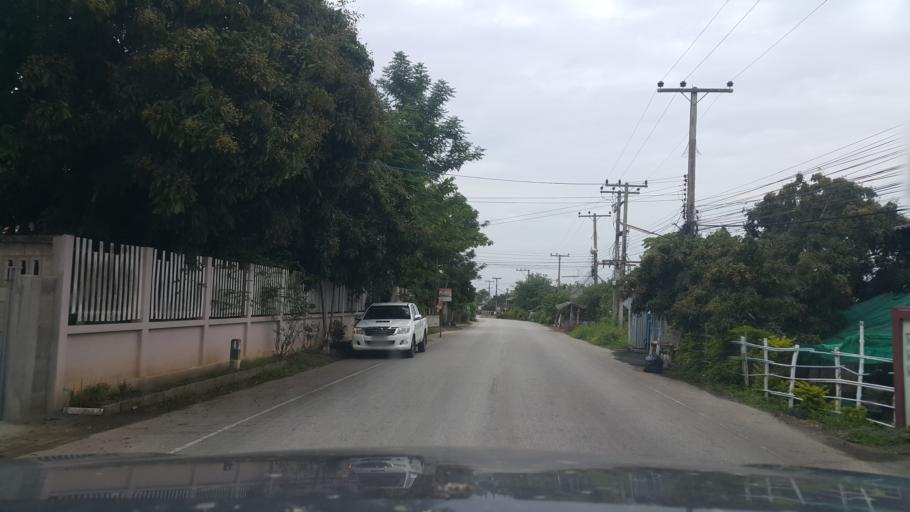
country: TH
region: Chiang Mai
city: San Pa Tong
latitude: 18.6522
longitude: 98.8375
